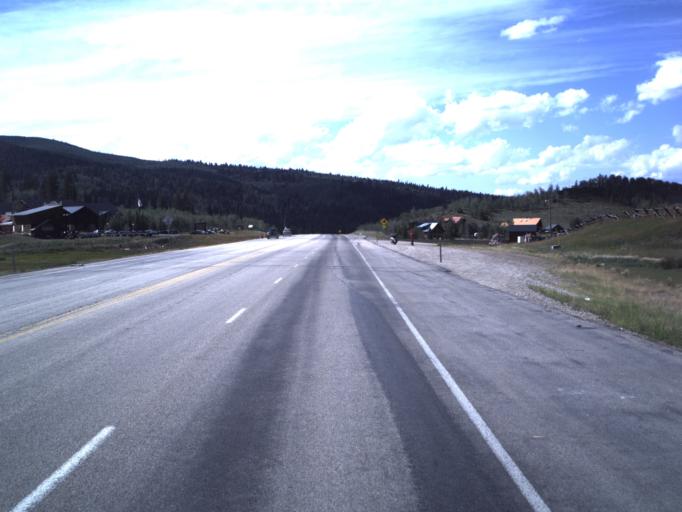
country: US
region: Utah
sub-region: Wasatch County
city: Heber
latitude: 40.2995
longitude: -111.2536
